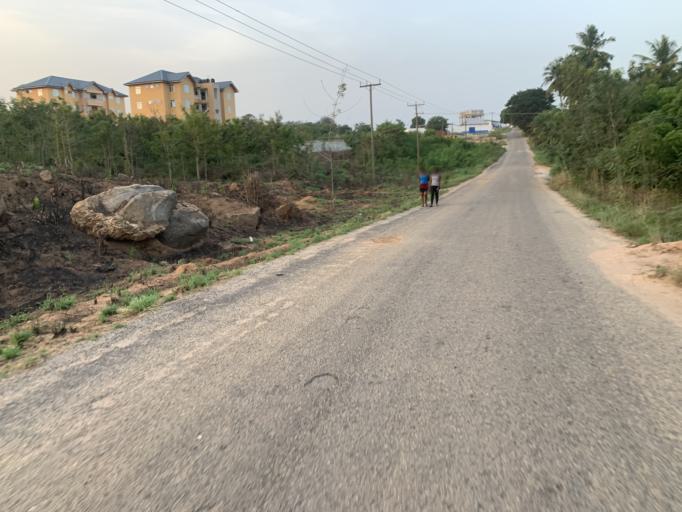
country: GH
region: Central
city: Winneba
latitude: 5.3646
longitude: -0.6203
